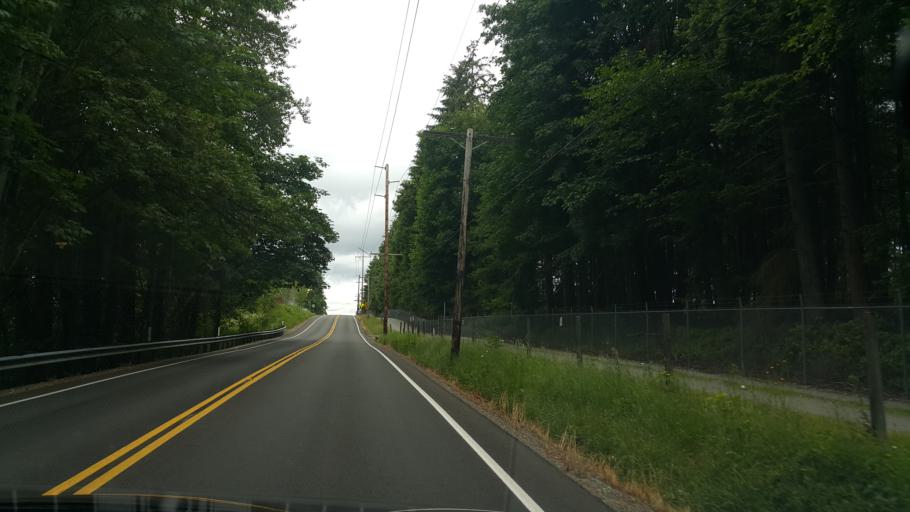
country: US
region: Washington
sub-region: King County
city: Fairwood
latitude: 47.4274
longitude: -122.1440
